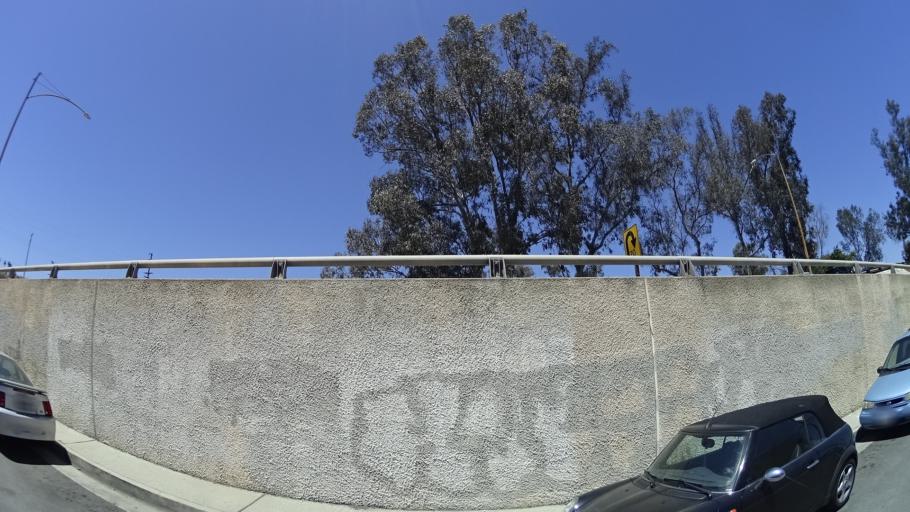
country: US
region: California
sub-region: Los Angeles County
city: Los Angeles
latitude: 34.0674
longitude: -118.2382
